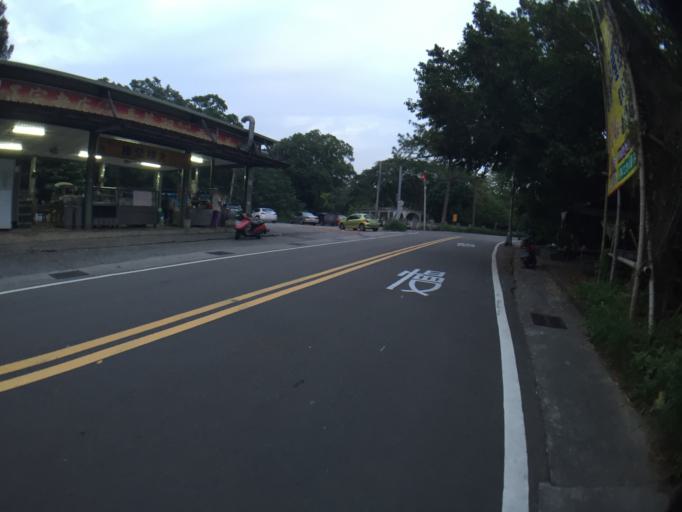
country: TW
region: Taiwan
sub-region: Hsinchu
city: Hsinchu
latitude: 24.7730
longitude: 120.9710
